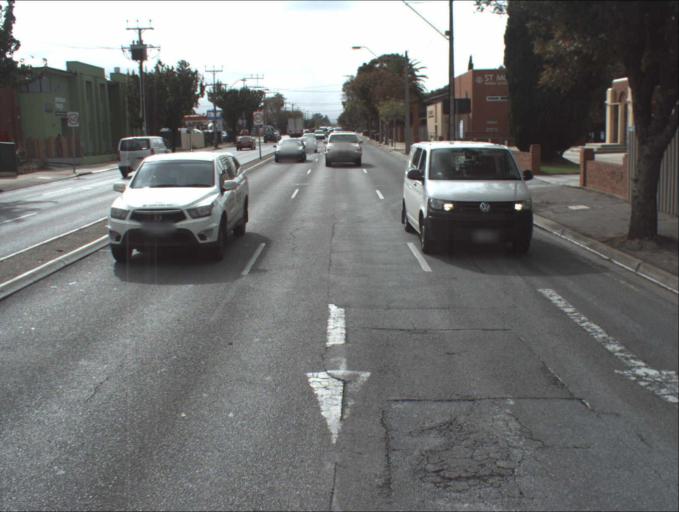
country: AU
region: South Australia
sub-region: Port Adelaide Enfield
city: Klemzig
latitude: -34.8878
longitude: 138.6153
